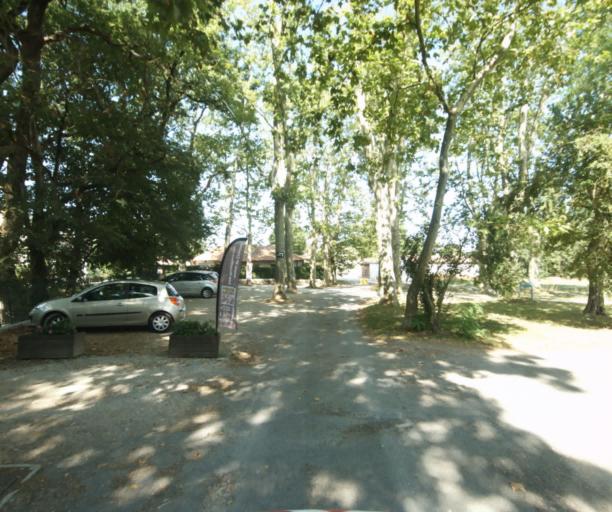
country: FR
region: Midi-Pyrenees
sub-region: Departement de la Haute-Garonne
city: Revel
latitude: 43.4970
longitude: 1.9687
